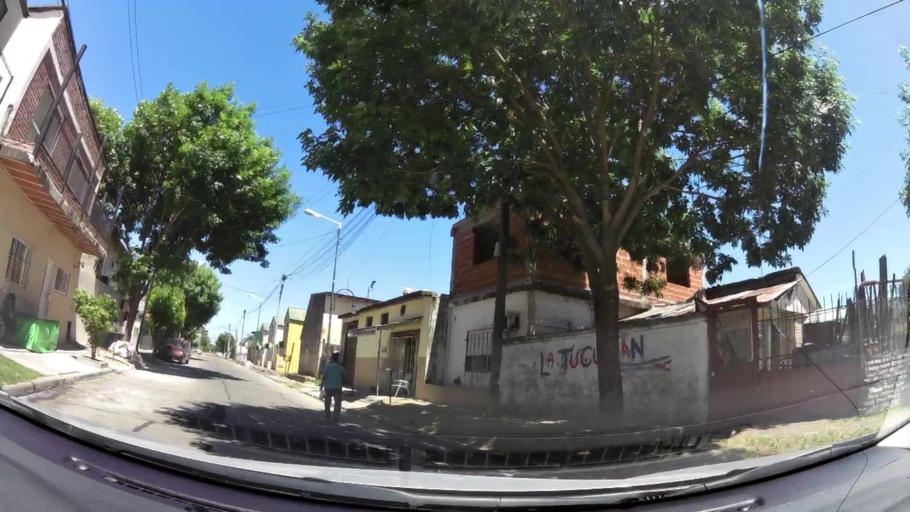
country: AR
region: Buenos Aires
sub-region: Partido de Tigre
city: Tigre
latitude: -34.4549
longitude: -58.5567
